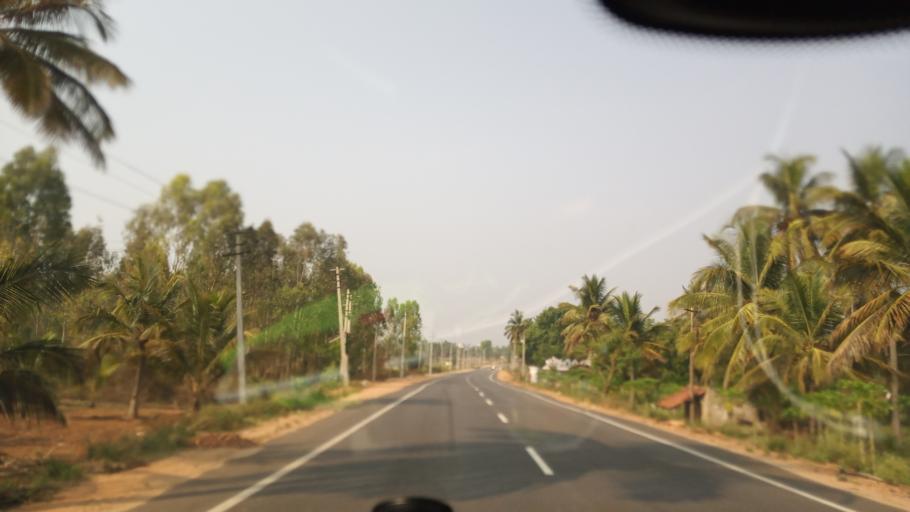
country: IN
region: Karnataka
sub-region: Mandya
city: Melukote
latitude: 12.7162
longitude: 76.7080
